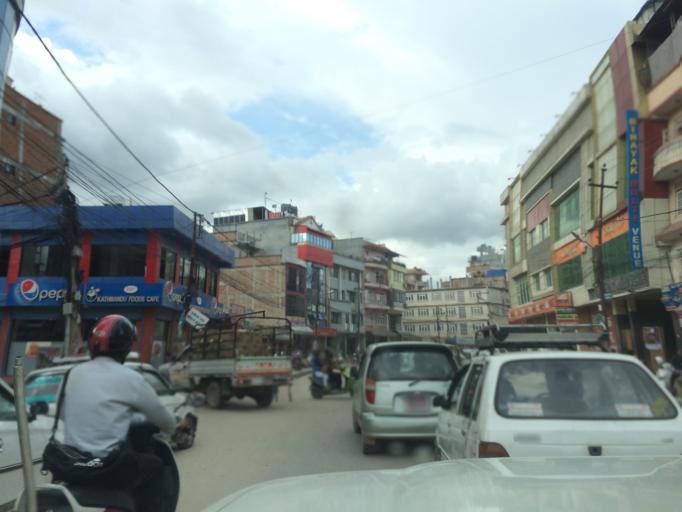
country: NP
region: Central Region
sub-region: Bagmati Zone
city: Kathmandu
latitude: 27.7158
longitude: 85.3038
